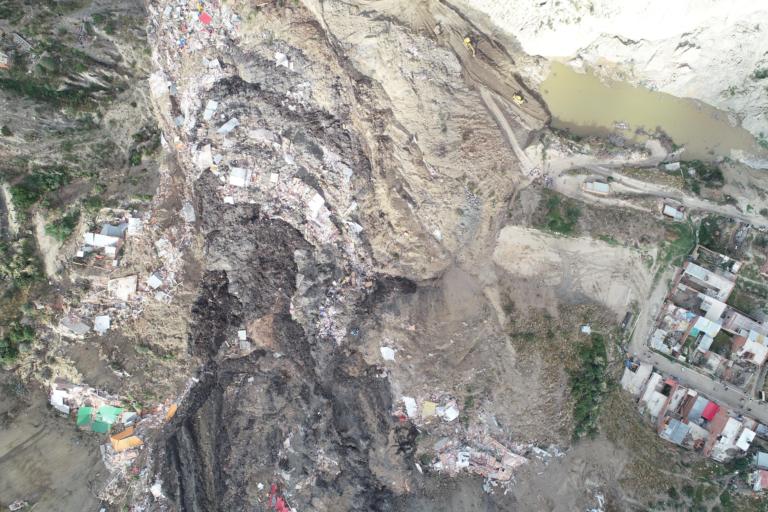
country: BO
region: La Paz
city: La Paz
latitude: -16.5193
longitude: -68.1221
